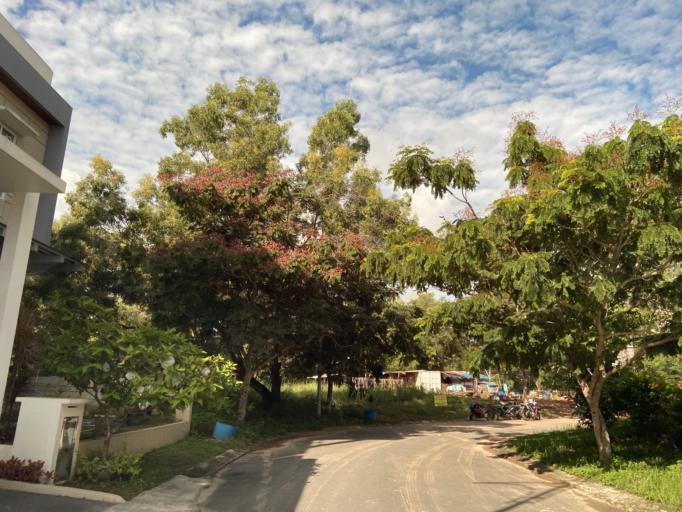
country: SG
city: Singapore
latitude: 1.0930
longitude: 104.0309
